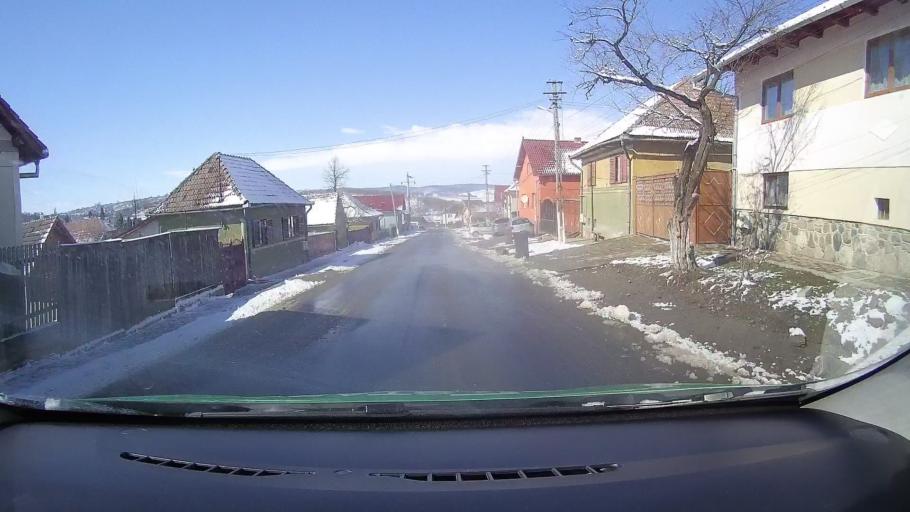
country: RO
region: Sibiu
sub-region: Comuna Rosia
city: Rosia
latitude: 45.8026
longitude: 24.2910
